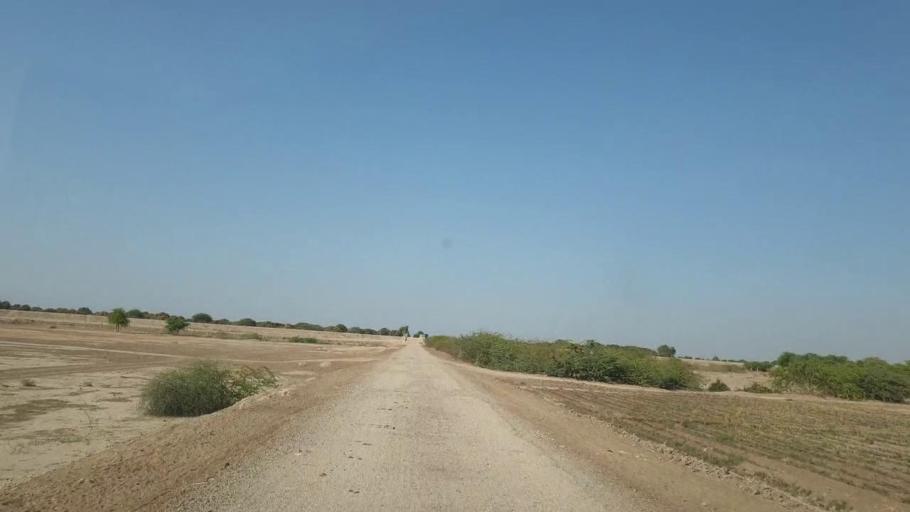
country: PK
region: Sindh
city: Nabisar
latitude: 25.0320
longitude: 69.4867
